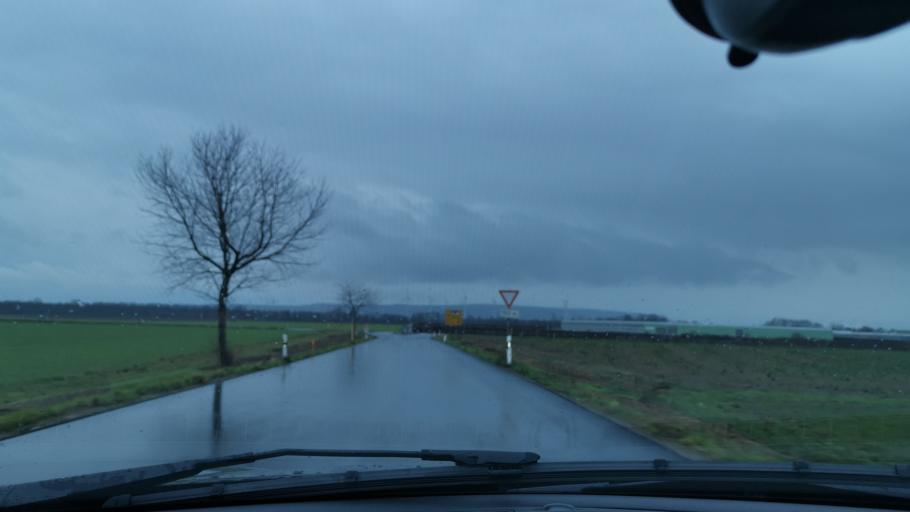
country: DE
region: North Rhine-Westphalia
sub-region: Regierungsbezirk Koln
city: Titz
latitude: 51.0063
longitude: 6.4979
